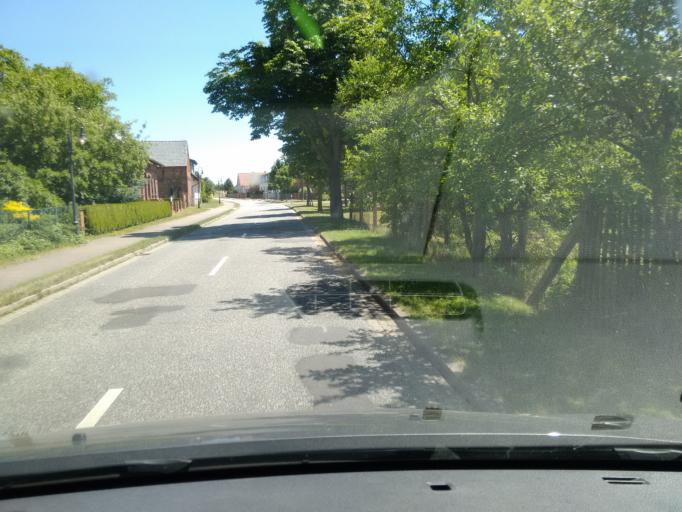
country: DE
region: Brandenburg
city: Beeskow
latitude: 52.1950
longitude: 14.3055
